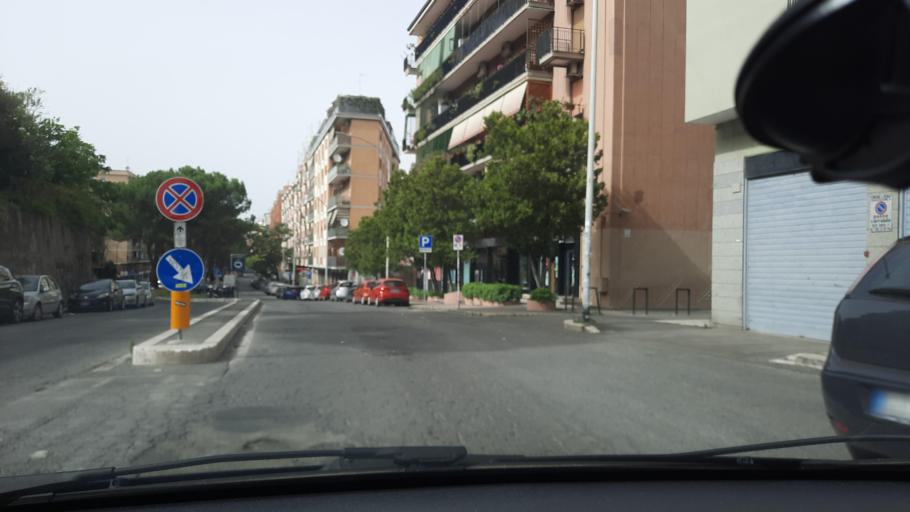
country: IT
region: Latium
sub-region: Citta metropolitana di Roma Capitale
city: Rome
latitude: 41.8537
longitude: 12.4804
